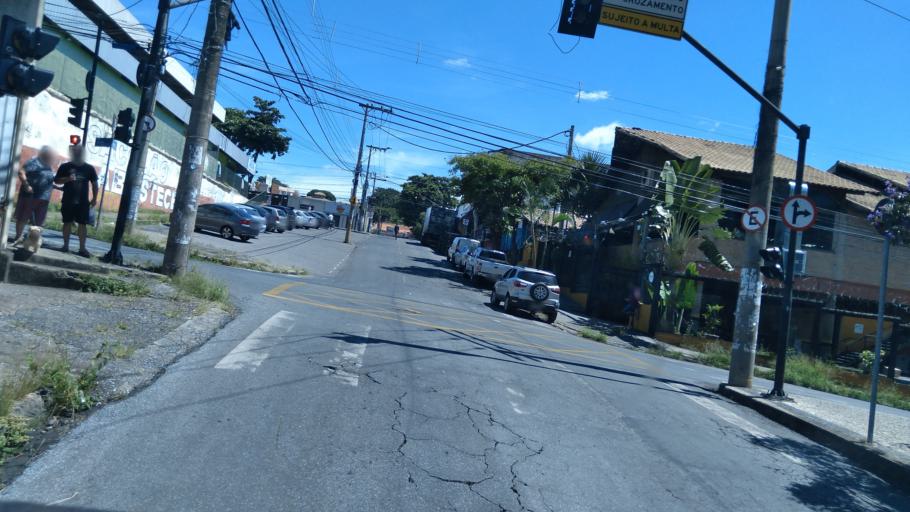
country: BR
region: Minas Gerais
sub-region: Belo Horizonte
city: Belo Horizonte
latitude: -19.9152
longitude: -43.9882
